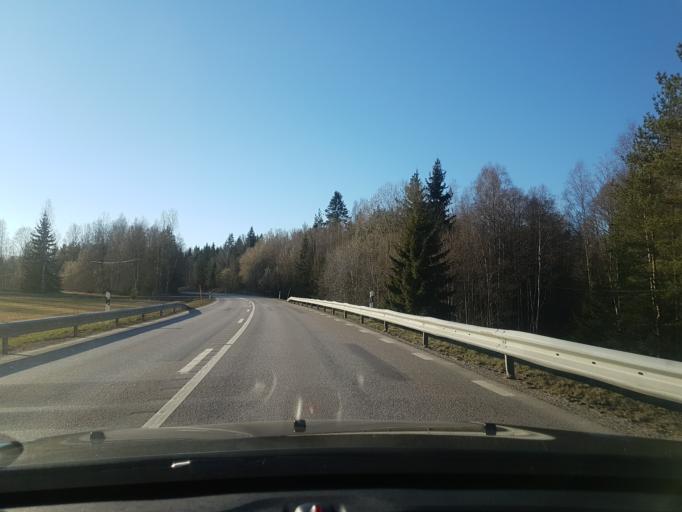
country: SE
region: Uppsala
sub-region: Heby Kommun
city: Morgongava
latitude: 59.9164
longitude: 17.0242
